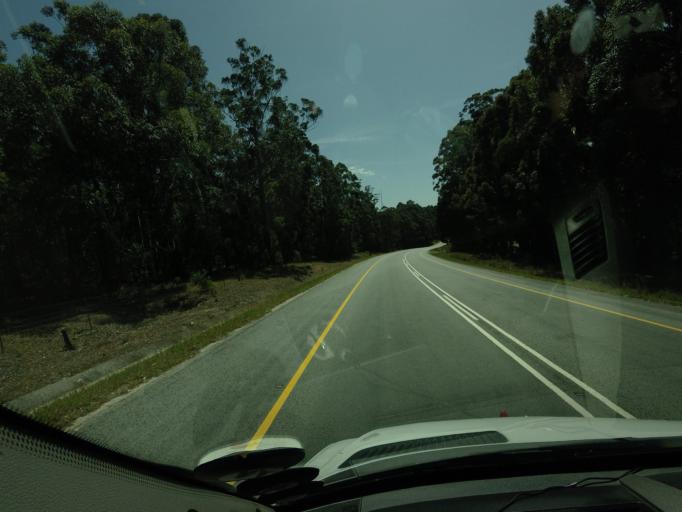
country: ZA
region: Western Cape
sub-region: Overberg District Municipality
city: Hermanus
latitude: -34.3066
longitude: 19.1330
